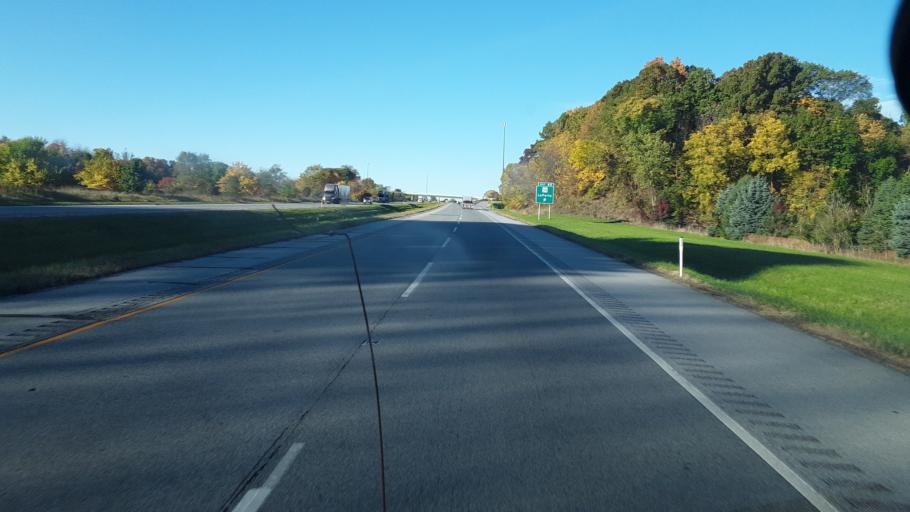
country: US
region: Indiana
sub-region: LaPorte County
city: LaPorte
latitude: 41.6693
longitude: -86.7245
